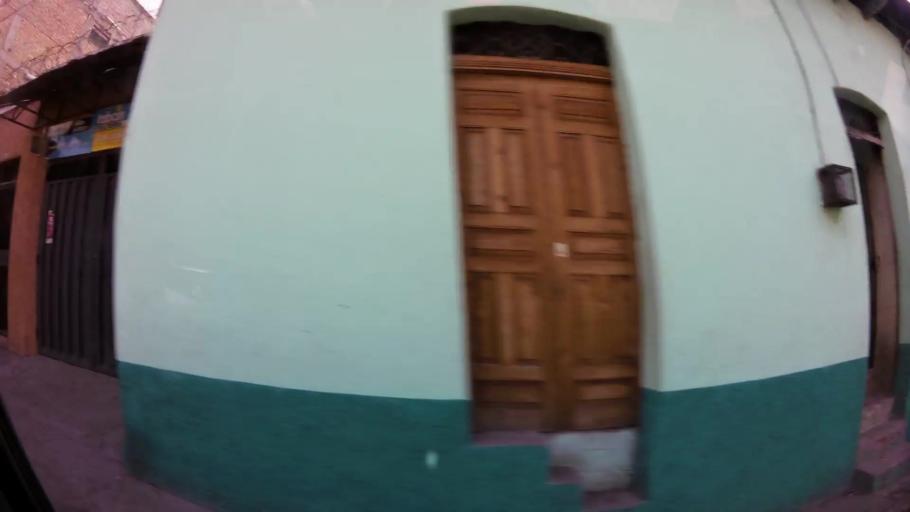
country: HN
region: Francisco Morazan
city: Tegucigalpa
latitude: 14.1011
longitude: -87.2021
